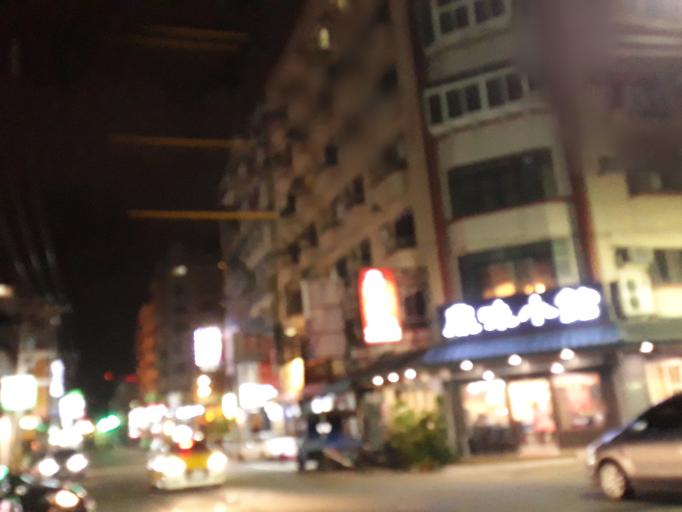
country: TW
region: Taiwan
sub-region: Hsinchu
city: Hsinchu
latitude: 24.8154
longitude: 120.9769
